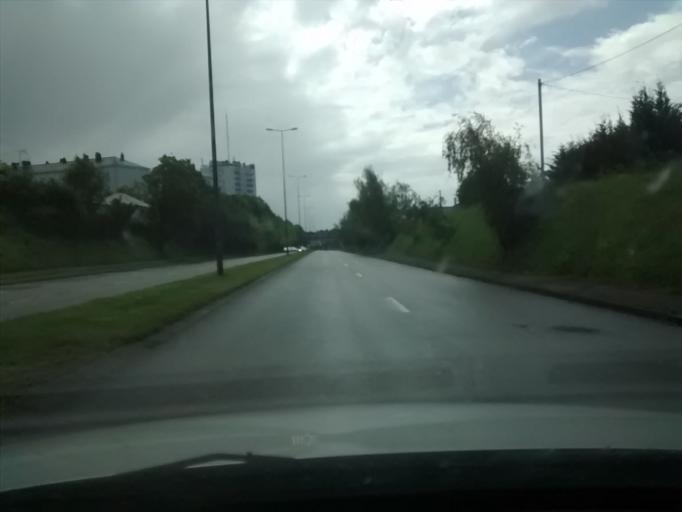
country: FR
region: Pays de la Loire
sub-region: Departement de la Mayenne
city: Laval
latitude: 48.0683
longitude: -0.7909
